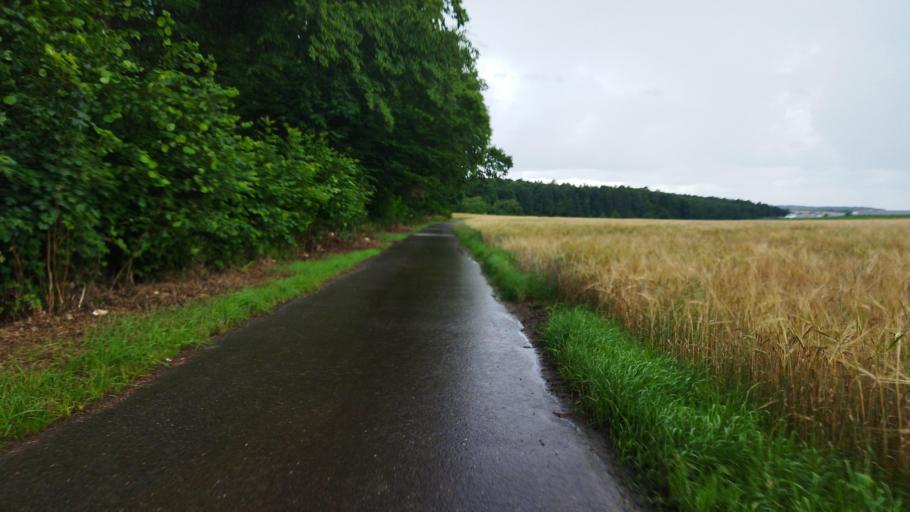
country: DE
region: Baden-Wuerttemberg
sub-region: Regierungsbezirk Stuttgart
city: Kirchardt
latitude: 49.2031
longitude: 9.0220
